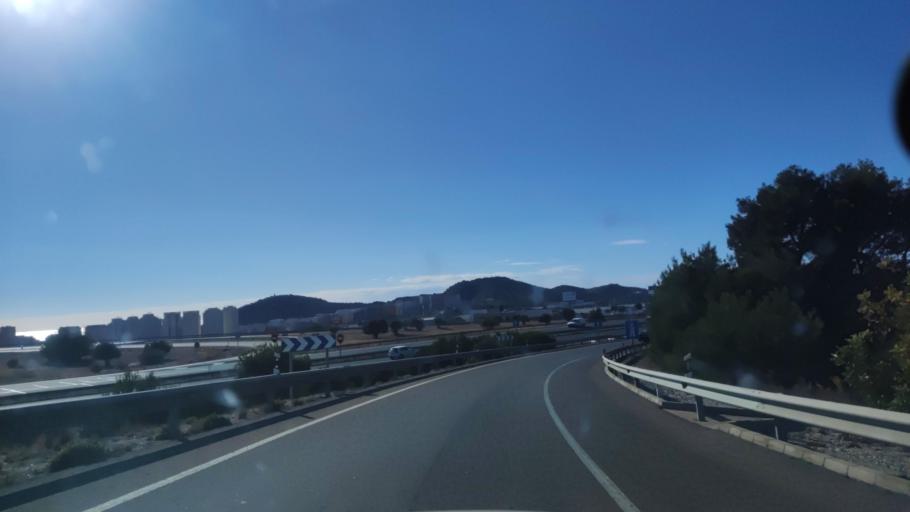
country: ES
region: Valencia
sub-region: Provincia de Alicante
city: Benidorm
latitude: 38.5438
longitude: -0.1722
